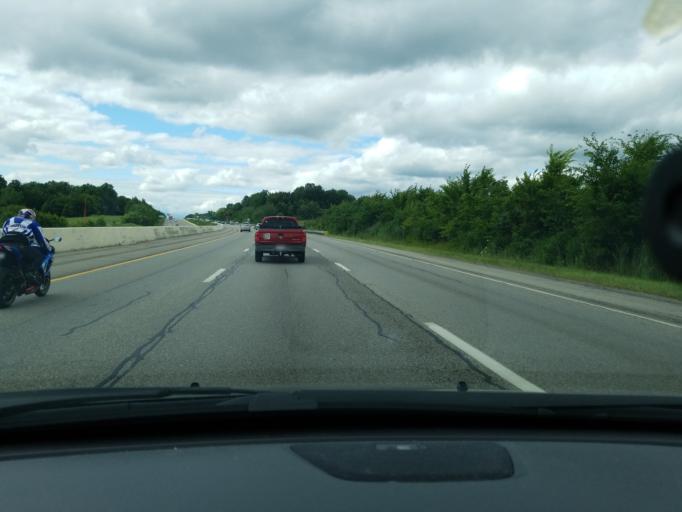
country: US
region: Ohio
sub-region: Stark County
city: Greentown
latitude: 40.9229
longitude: -81.4279
